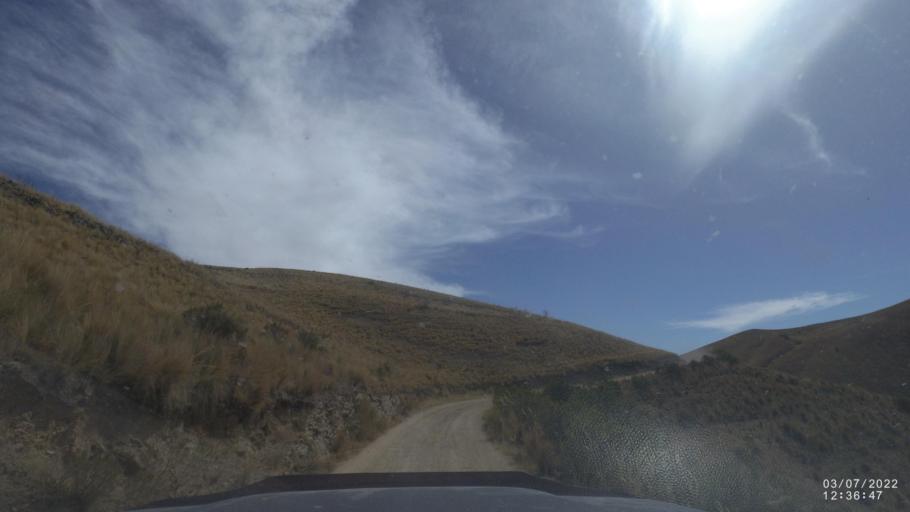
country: BO
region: Cochabamba
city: Irpa Irpa
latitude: -17.7999
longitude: -66.6141
